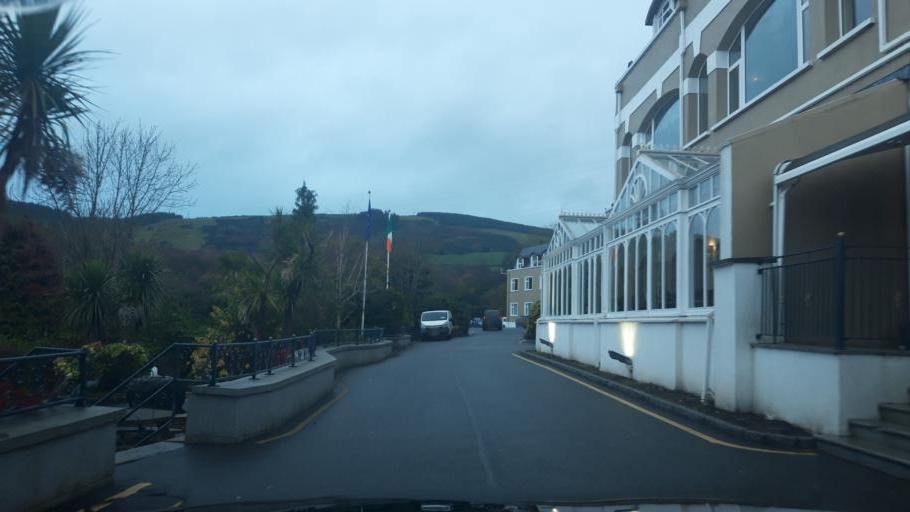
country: IE
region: Leinster
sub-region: Wicklow
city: Kilmacanoge
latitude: 53.1423
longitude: -6.1266
